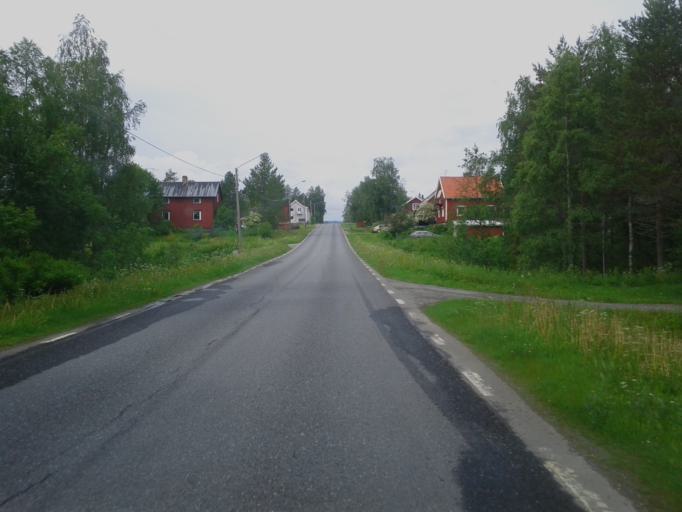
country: SE
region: Vaesterbotten
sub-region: Skelleftea Kommun
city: Forsbacka
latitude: 64.9086
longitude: 20.6170
